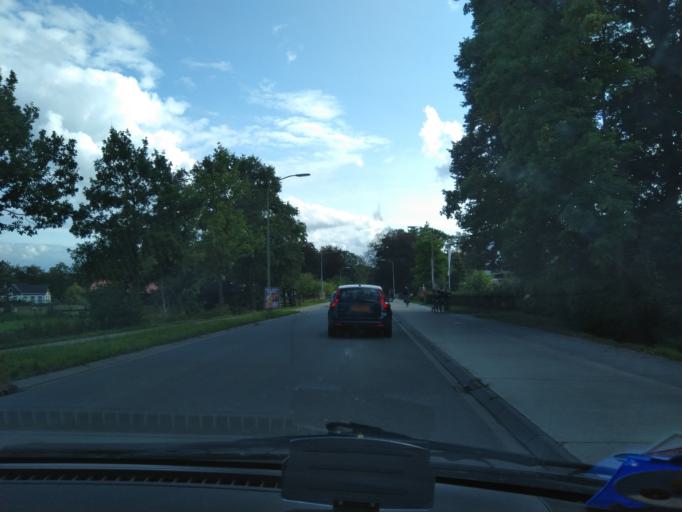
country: NL
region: Groningen
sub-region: Gemeente Haren
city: Haren
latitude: 53.1565
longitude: 6.5640
